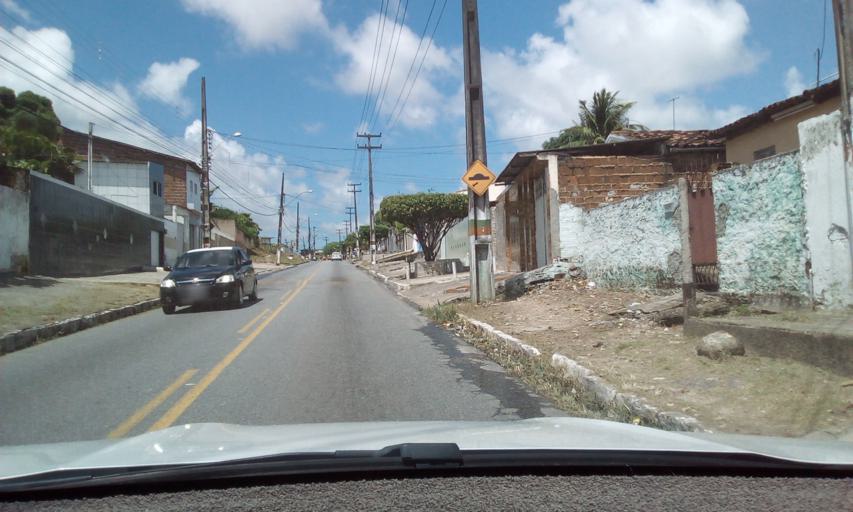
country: BR
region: Paraiba
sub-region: Bayeux
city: Bayeux
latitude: -7.1247
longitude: -34.9326
